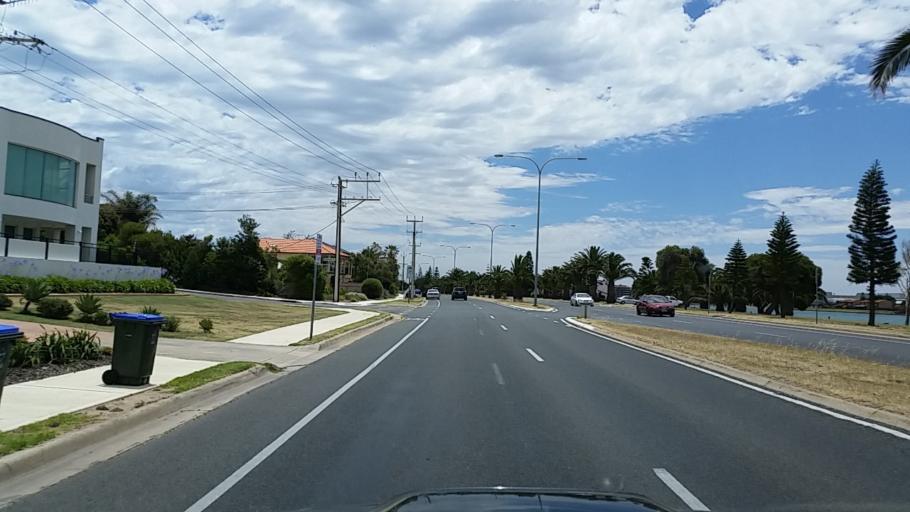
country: AU
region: South Australia
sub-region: Charles Sturt
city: Grange
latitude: -34.8874
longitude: 138.4869
